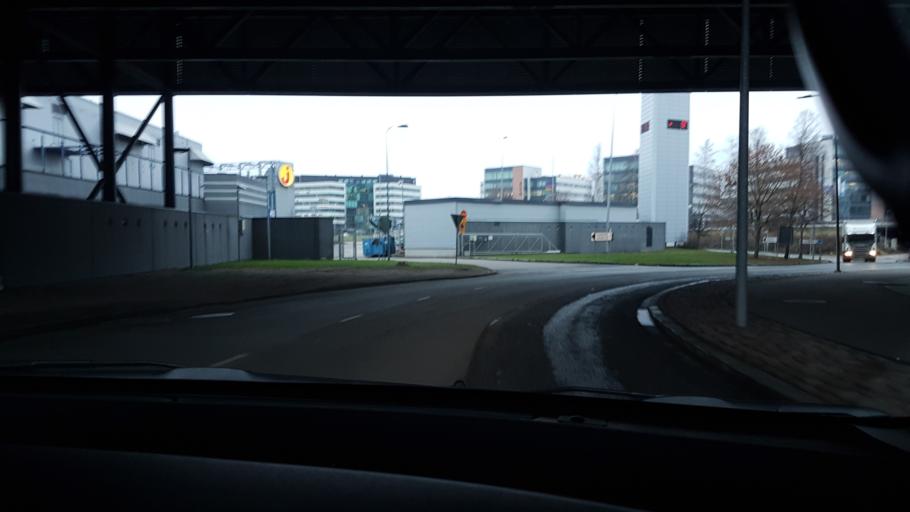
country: FI
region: Uusimaa
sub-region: Helsinki
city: Vantaa
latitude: 60.2908
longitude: 24.9676
